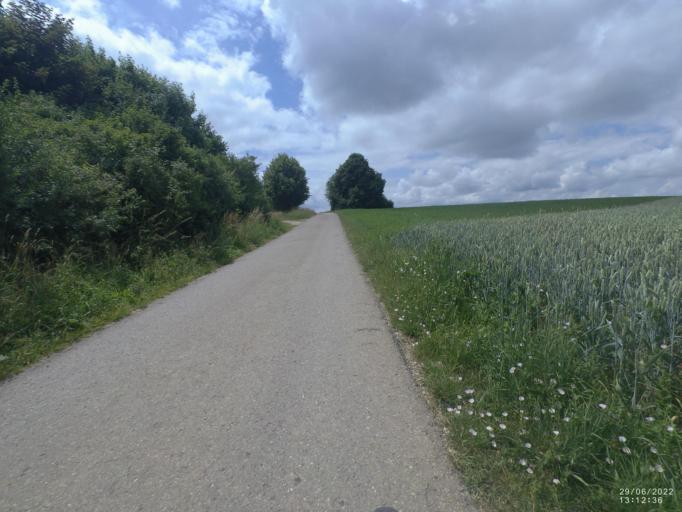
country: DE
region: Baden-Wuerttemberg
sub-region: Regierungsbezirk Stuttgart
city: Gerstetten
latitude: 48.6378
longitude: 9.9767
